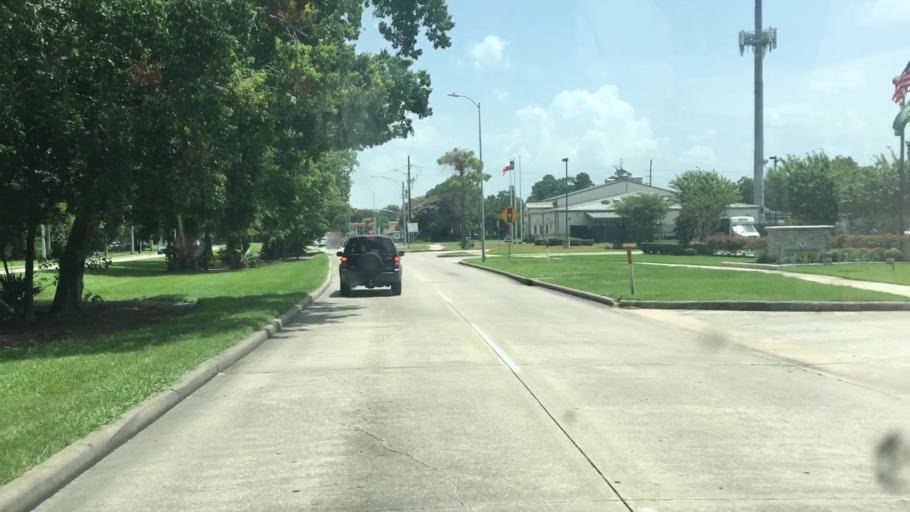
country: US
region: Texas
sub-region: Harris County
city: Atascocita
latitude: 29.9288
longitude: -95.1774
